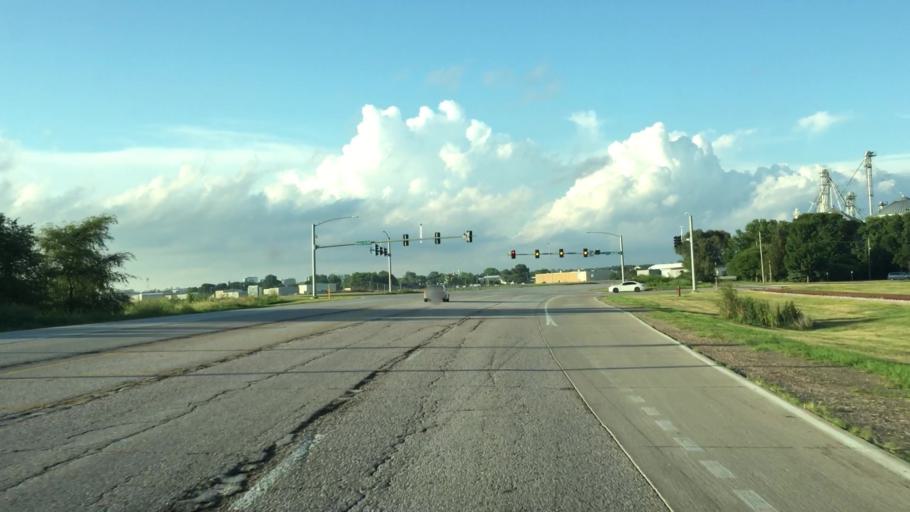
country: US
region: Iowa
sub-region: Johnson County
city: University Heights
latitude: 41.6305
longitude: -91.5430
